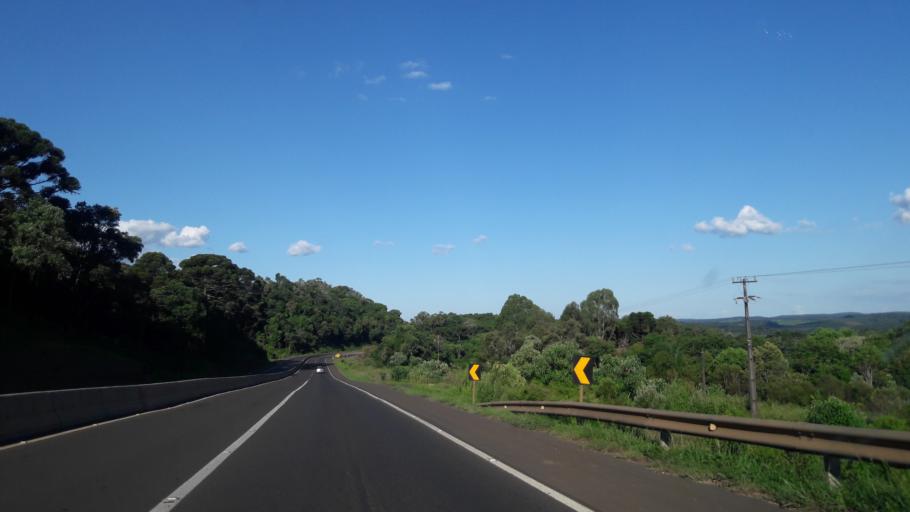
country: BR
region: Parana
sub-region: Guarapuava
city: Guarapuava
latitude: -25.3482
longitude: -51.3890
